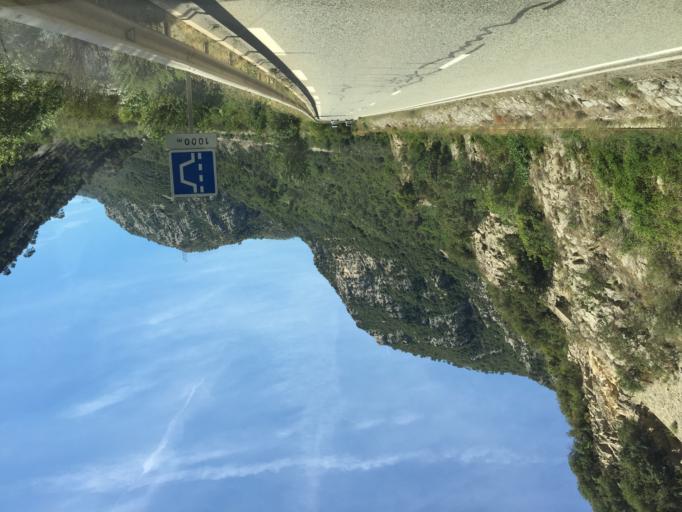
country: FR
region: Provence-Alpes-Cote d'Azur
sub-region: Departement des Alpes-Maritimes
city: Levens
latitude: 43.8728
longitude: 7.1951
